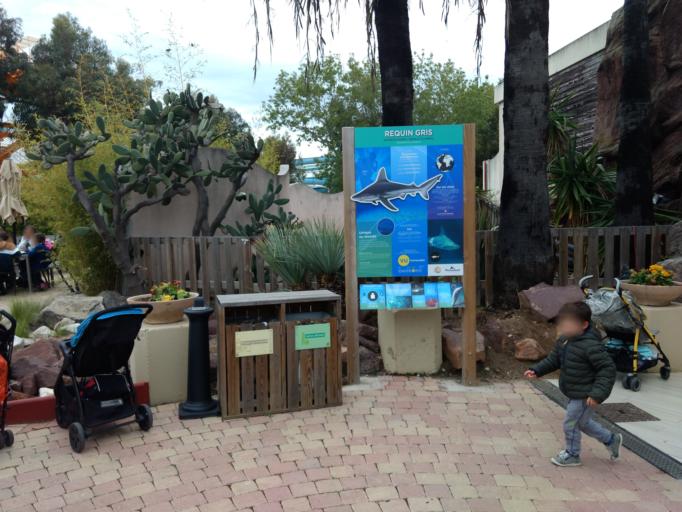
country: FR
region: Provence-Alpes-Cote d'Azur
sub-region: Departement des Alpes-Maritimes
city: Biot
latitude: 43.6154
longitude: 7.1258
